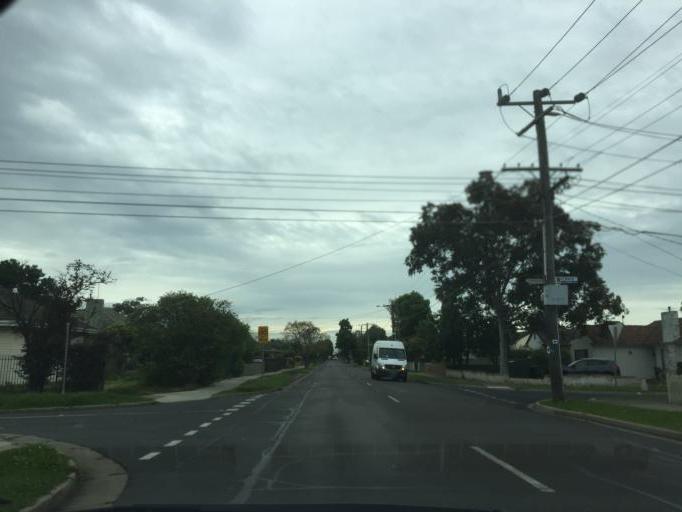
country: AU
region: Victoria
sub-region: Maribyrnong
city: Braybrook
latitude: -37.7810
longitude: 144.8469
